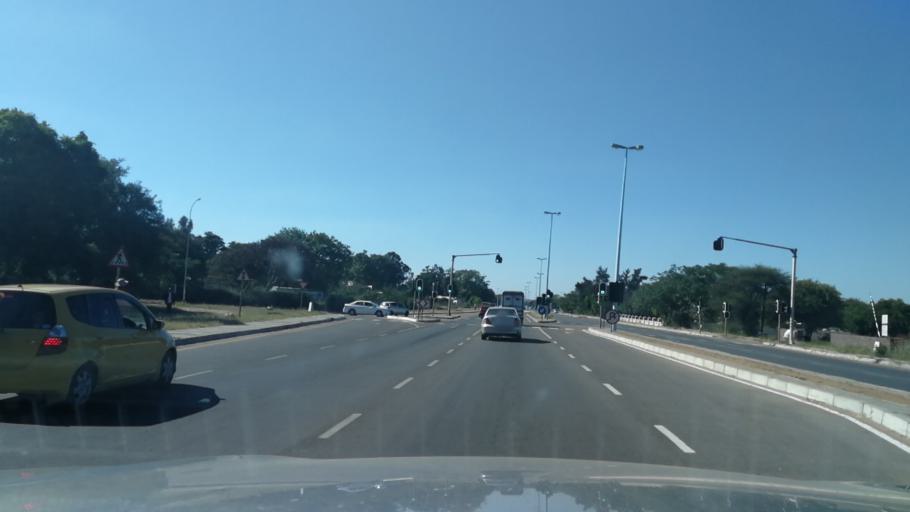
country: BW
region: South East
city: Gaborone
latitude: -24.6761
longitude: 25.9209
